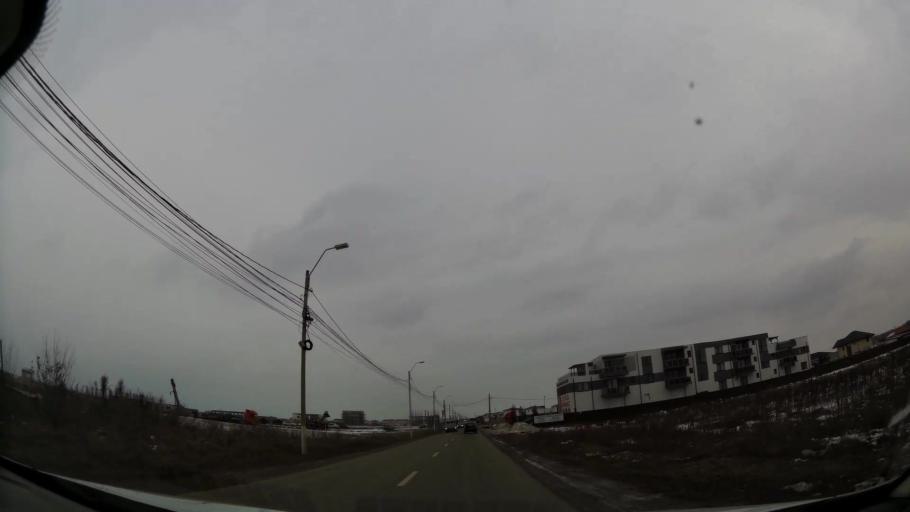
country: RO
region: Ilfov
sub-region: Comuna Tunari
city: Tunari
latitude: 44.5515
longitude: 26.1124
